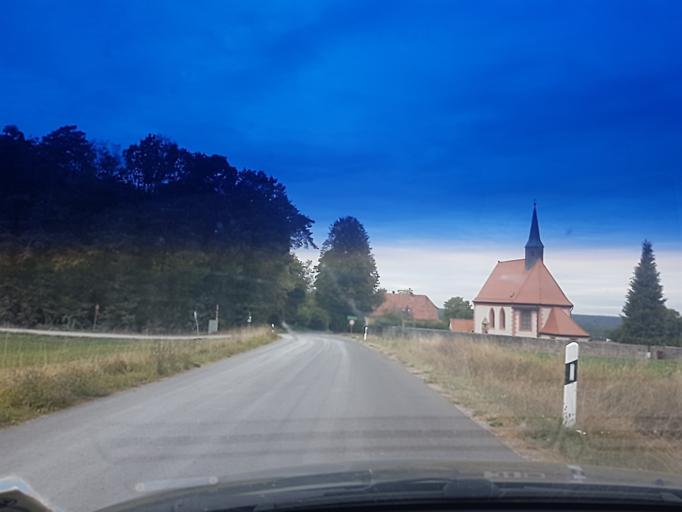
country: DE
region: Bavaria
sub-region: Regierungsbezirk Unterfranken
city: Geiselwind
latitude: 49.8255
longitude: 10.4861
